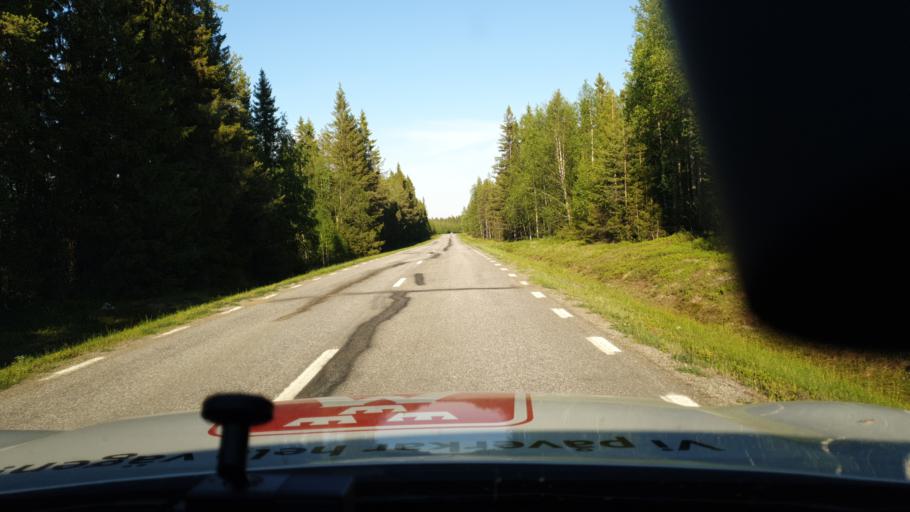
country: SE
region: Vaesterbotten
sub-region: Lycksele Kommun
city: Soderfors
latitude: 64.6232
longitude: 18.1118
